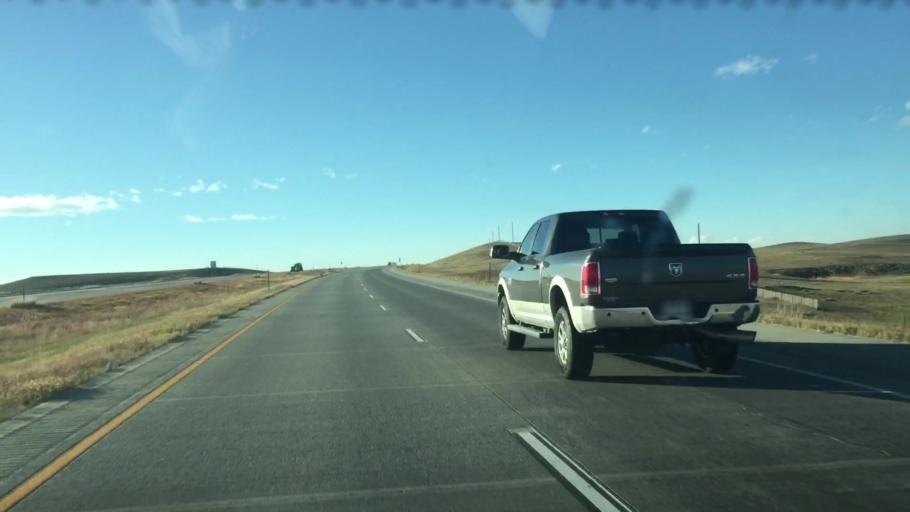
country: US
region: Colorado
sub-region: Lincoln County
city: Limon
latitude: 39.3031
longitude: -103.8155
